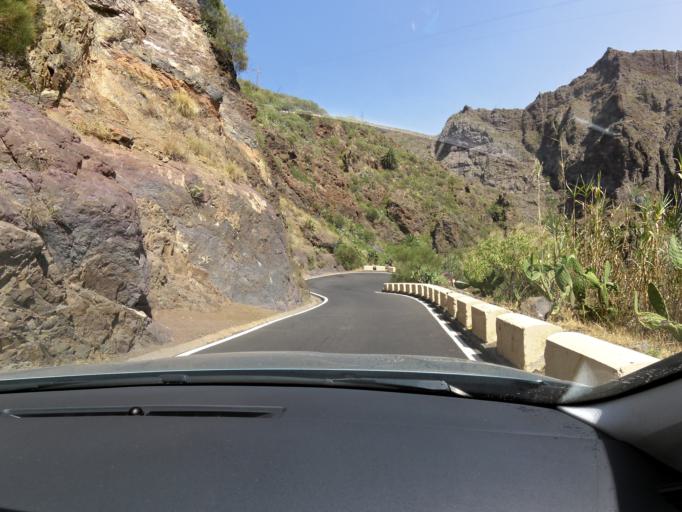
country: ES
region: Canary Islands
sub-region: Provincia de Santa Cruz de Tenerife
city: Santiago del Teide
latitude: 28.3042
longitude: -16.8351
